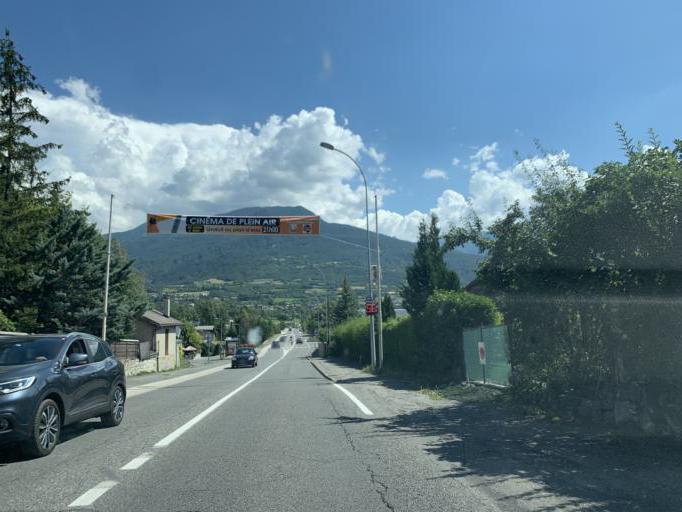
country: FR
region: Provence-Alpes-Cote d'Azur
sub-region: Departement des Hautes-Alpes
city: Embrun
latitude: 44.5534
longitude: 6.4837
